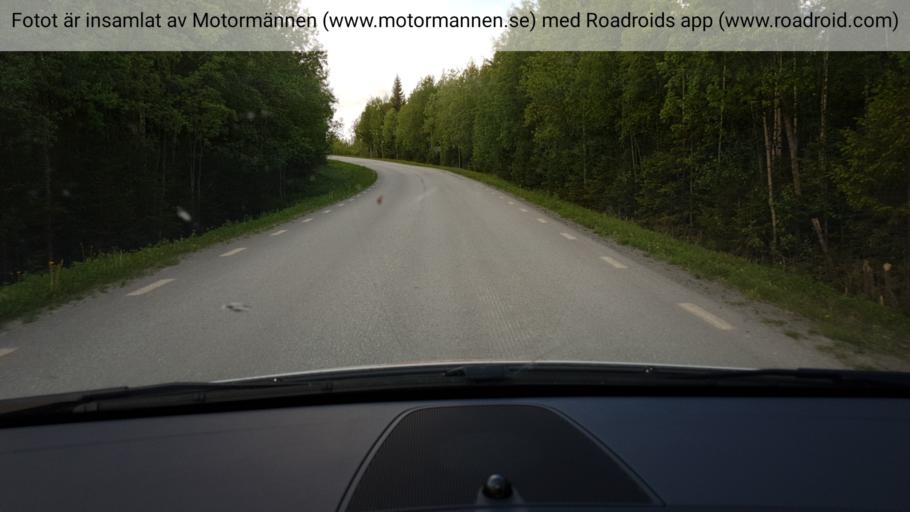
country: SE
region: Jaemtland
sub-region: Bergs Kommun
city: Hoverberg
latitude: 63.0427
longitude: 13.9985
